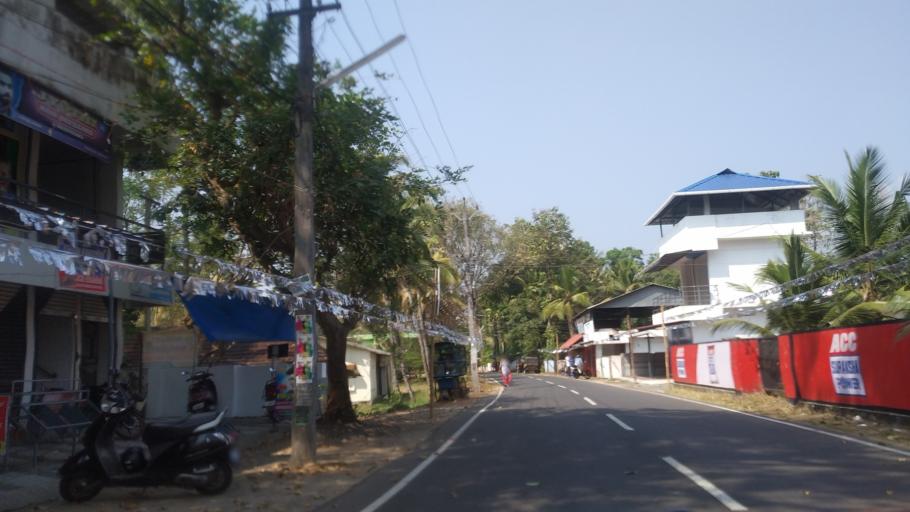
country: IN
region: Kerala
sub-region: Ernakulam
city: Elur
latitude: 10.1253
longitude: 76.2379
